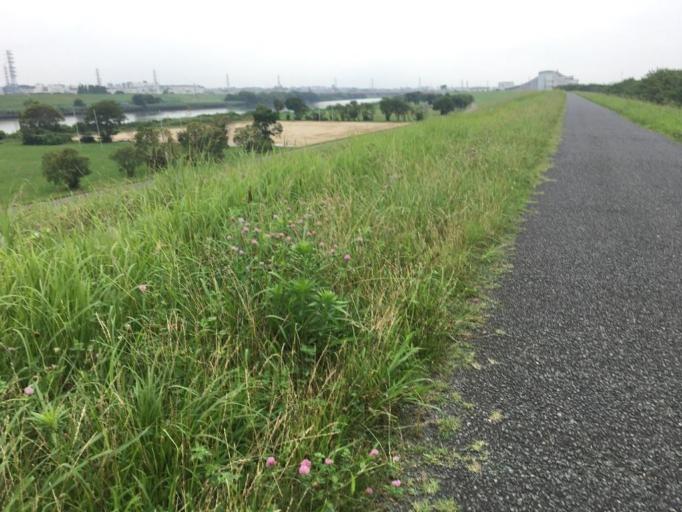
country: JP
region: Saitama
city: Shimotoda
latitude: 35.8023
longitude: 139.6681
